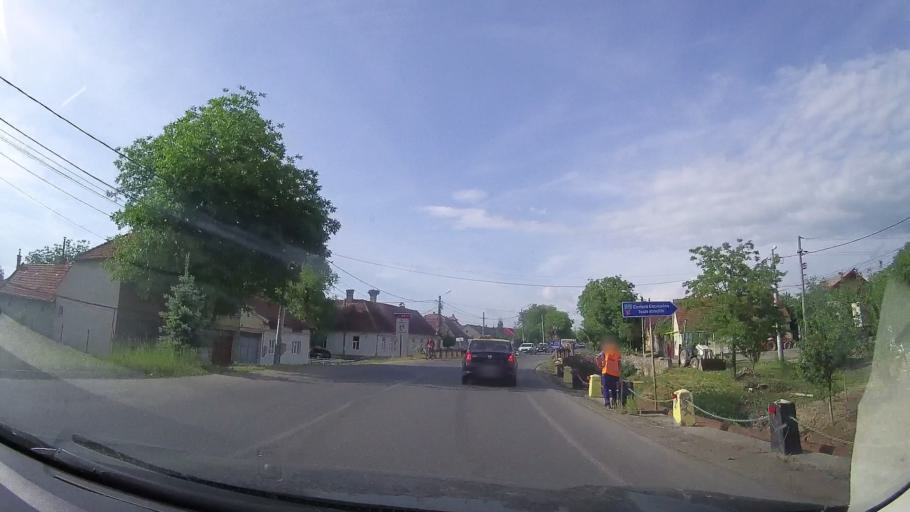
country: RO
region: Caras-Severin
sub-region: Municipiul Caransebes
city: Caransebes
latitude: 45.4021
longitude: 22.2240
